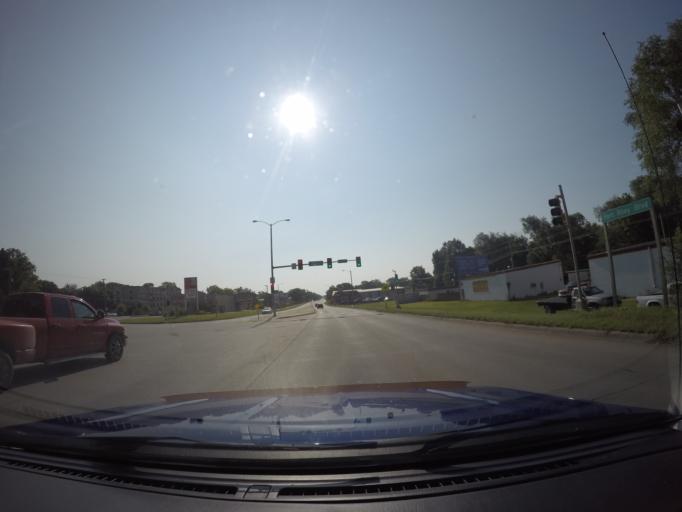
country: US
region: Kansas
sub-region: Riley County
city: Manhattan
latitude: 39.1743
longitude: -96.5847
